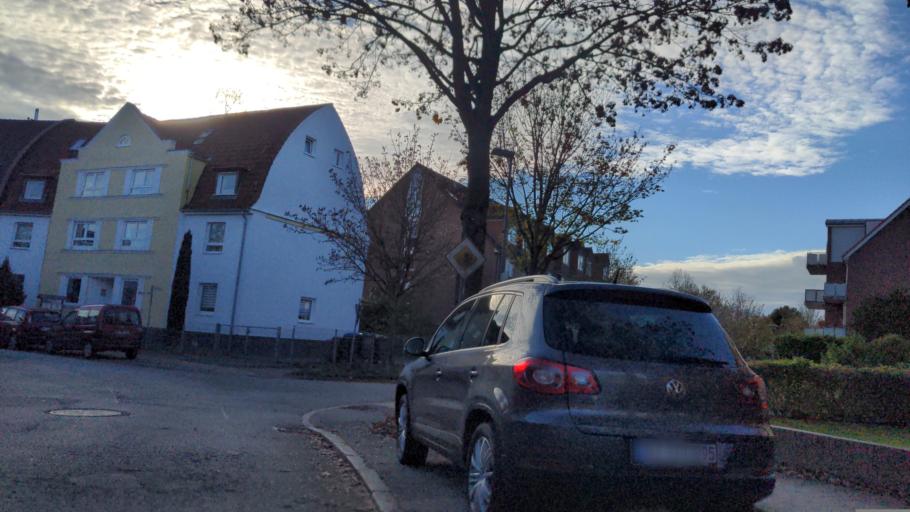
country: DE
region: Schleswig-Holstein
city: Luebeck
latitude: 53.8598
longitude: 10.6581
